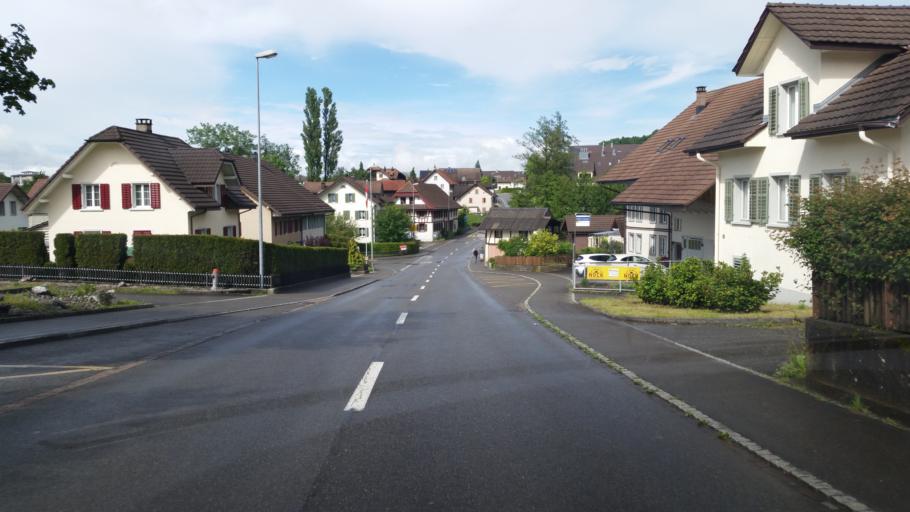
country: CH
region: Aargau
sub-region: Bezirk Bremgarten
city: Sarmenstorf
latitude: 47.3256
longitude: 8.2685
